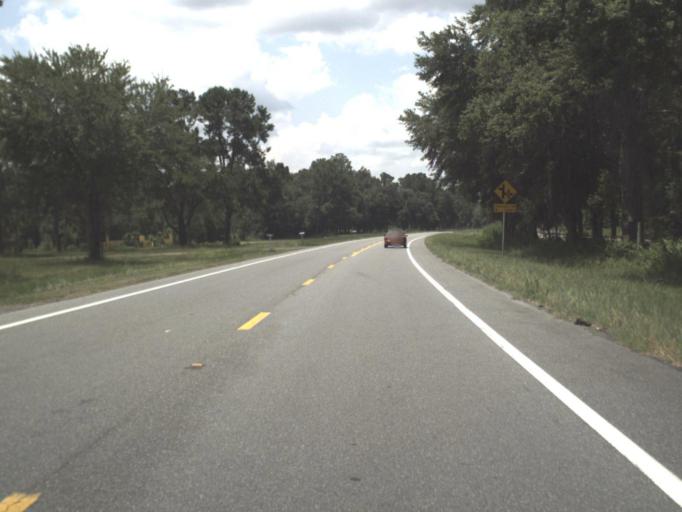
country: US
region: Florida
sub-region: Columbia County
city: Five Points
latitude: 30.2841
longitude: -82.7020
